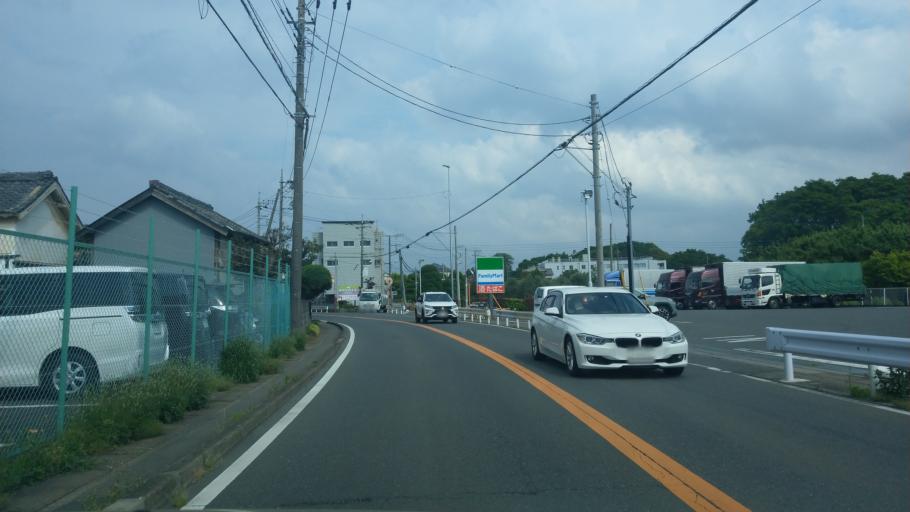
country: JP
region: Saitama
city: Saitama
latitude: 35.9040
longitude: 139.6827
